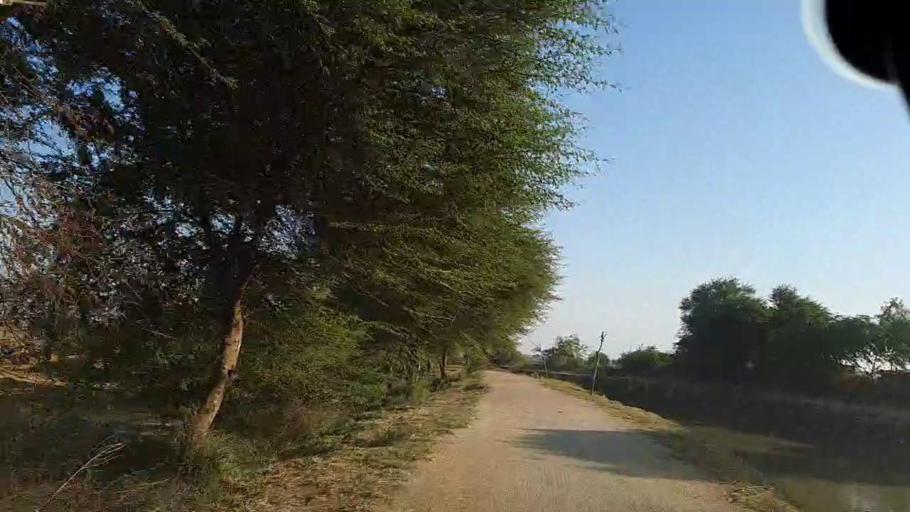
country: PK
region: Sindh
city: Chuhar Jamali
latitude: 24.5622
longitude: 68.0689
